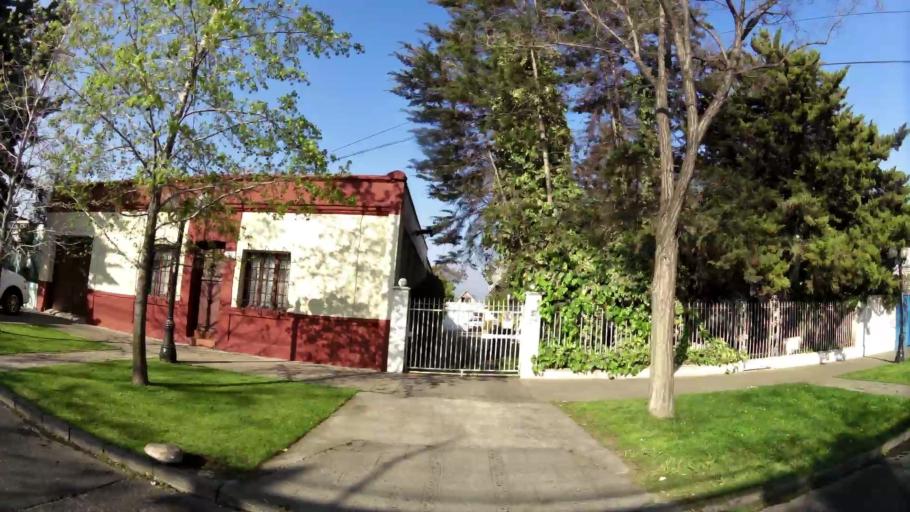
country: CL
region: Santiago Metropolitan
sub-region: Provincia de Santiago
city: Villa Presidente Frei, Nunoa, Santiago, Chile
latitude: -33.4417
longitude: -70.5977
